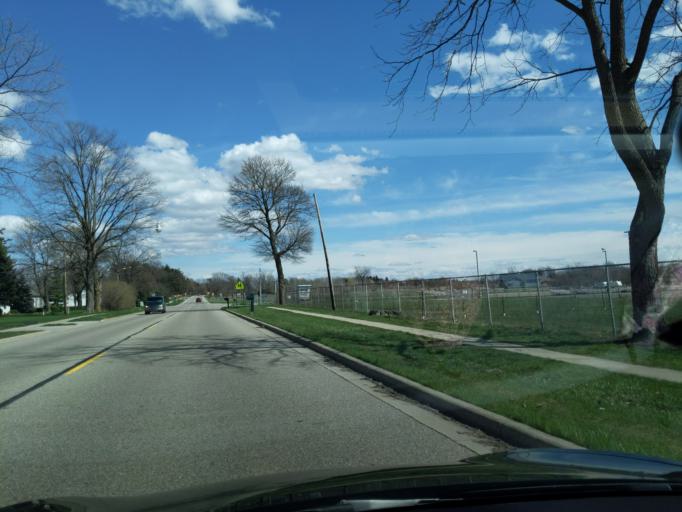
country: US
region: Michigan
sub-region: Ingham County
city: Mason
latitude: 42.5777
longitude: -84.4293
